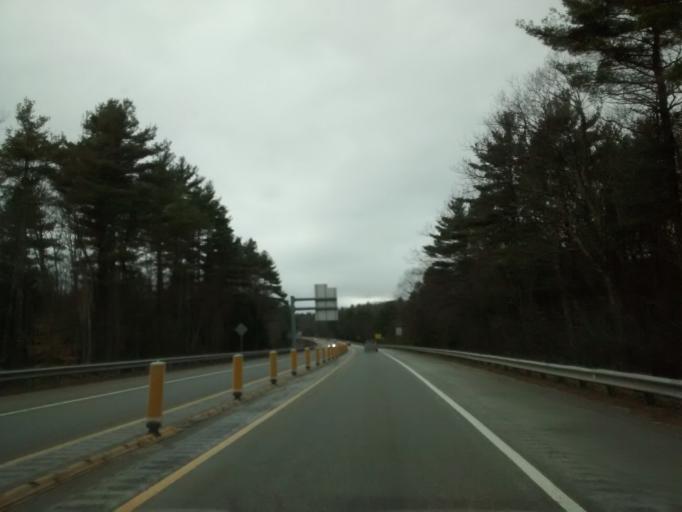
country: US
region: Massachusetts
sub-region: Worcester County
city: Phillipston
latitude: 42.5724
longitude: -72.1353
